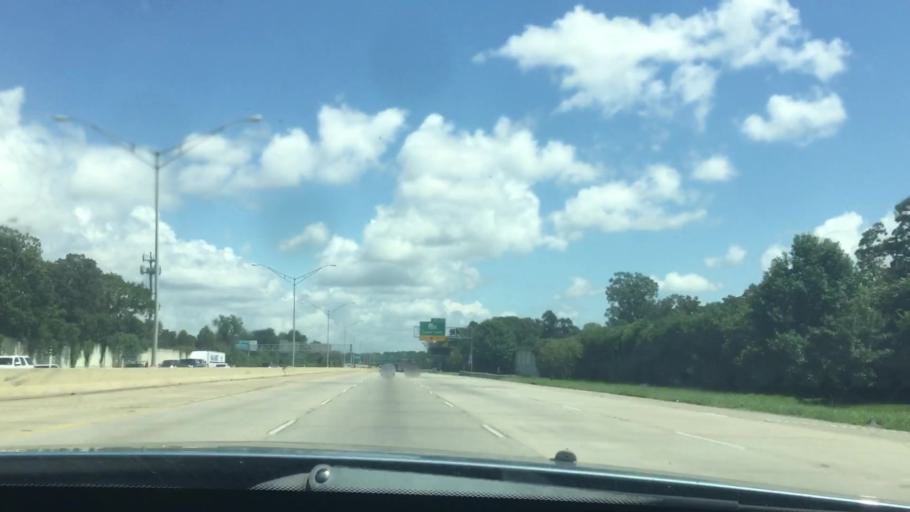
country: US
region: Louisiana
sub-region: East Baton Rouge Parish
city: Westminster
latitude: 30.4181
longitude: -91.1099
